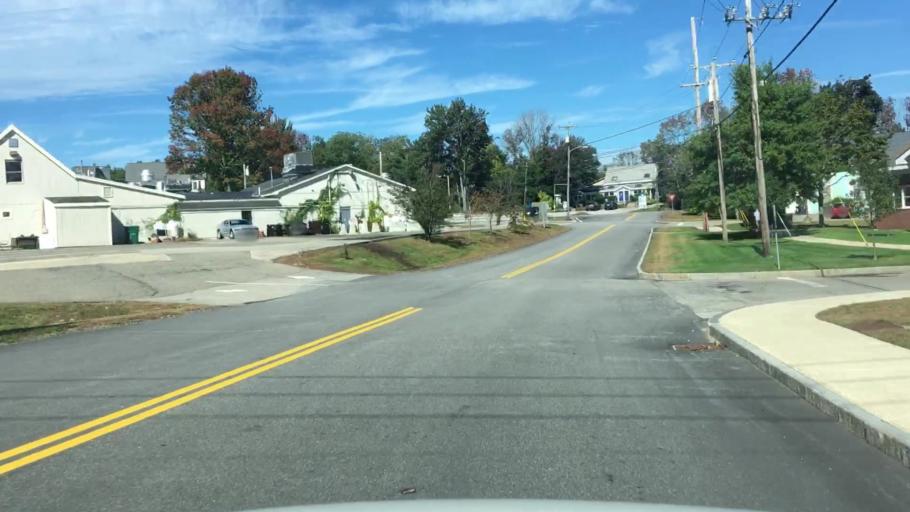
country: US
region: Maine
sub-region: York County
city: Kittery
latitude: 43.1011
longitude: -70.7425
